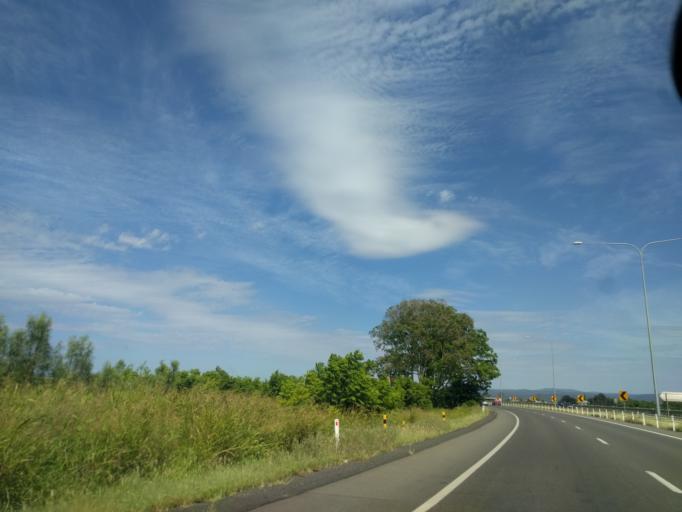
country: AU
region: Queensland
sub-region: Lockyer Valley
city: Gatton
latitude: -27.5427
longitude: 152.3758
